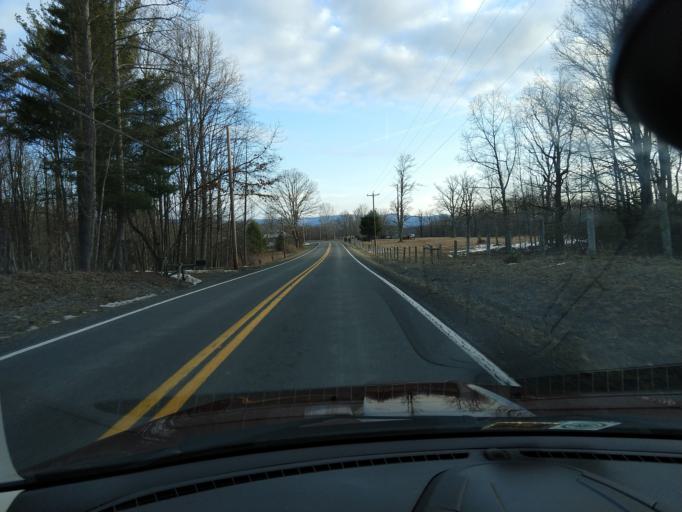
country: US
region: West Virginia
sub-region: Pocahontas County
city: Marlinton
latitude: 38.0874
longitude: -80.2785
